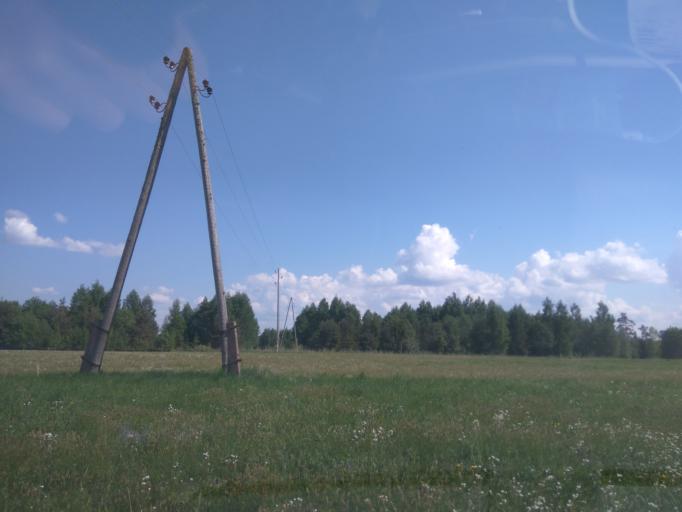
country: LV
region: Kuldigas Rajons
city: Kuldiga
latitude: 57.1759
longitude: 22.0133
